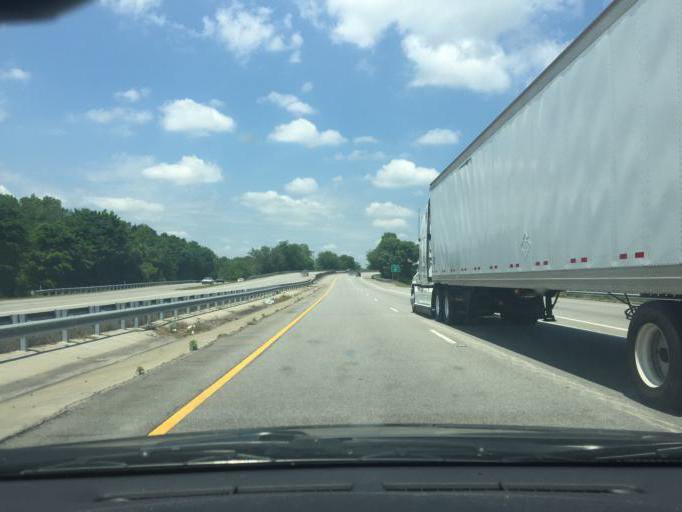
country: US
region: Georgia
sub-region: Chatham County
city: Thunderbolt
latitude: 32.0525
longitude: -81.0702
